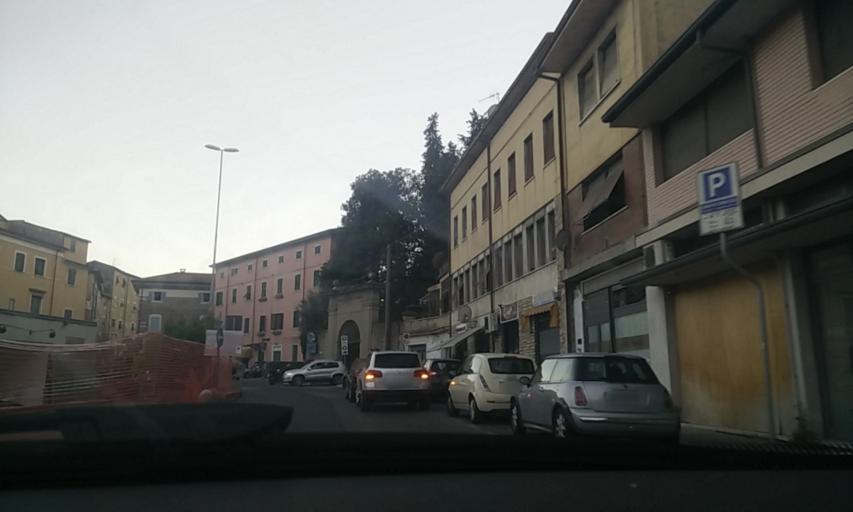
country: IT
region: Tuscany
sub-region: Provincia di Massa-Carrara
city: Carrara
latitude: 44.0791
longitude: 10.0951
